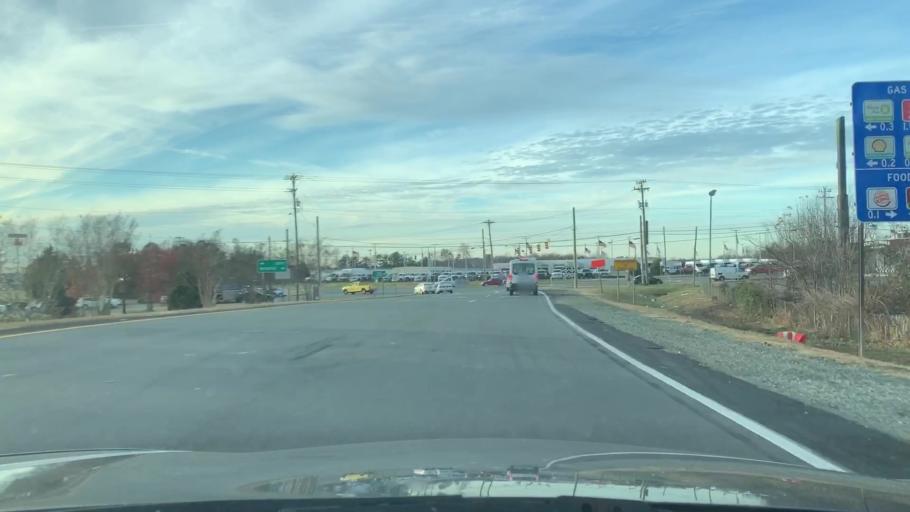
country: US
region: North Carolina
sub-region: Alamance County
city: Graham
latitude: 36.0643
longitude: -79.4297
